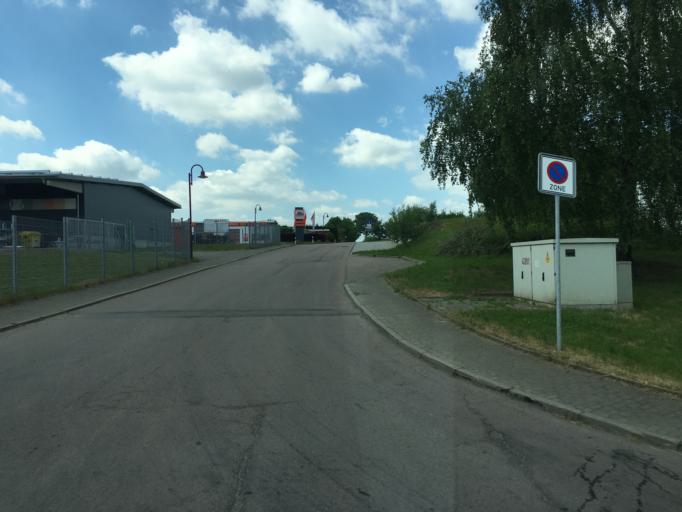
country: DE
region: Saxony
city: Hainichen
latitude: 50.9994
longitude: 13.1246
